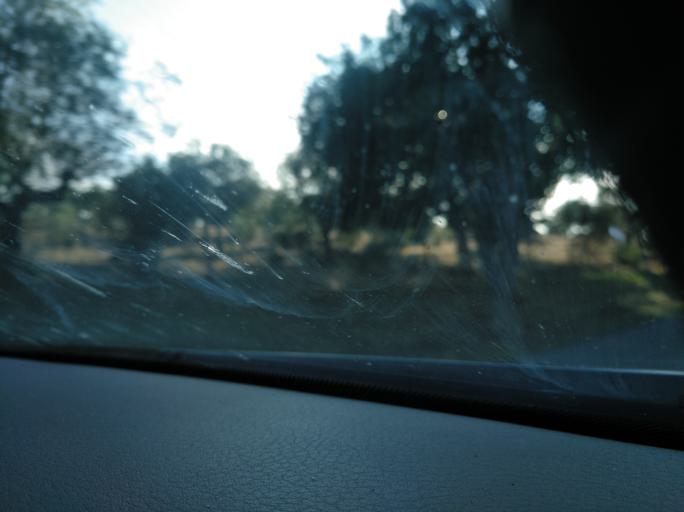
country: PT
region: Evora
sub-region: Borba
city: Borba
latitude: 38.9437
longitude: -7.4784
